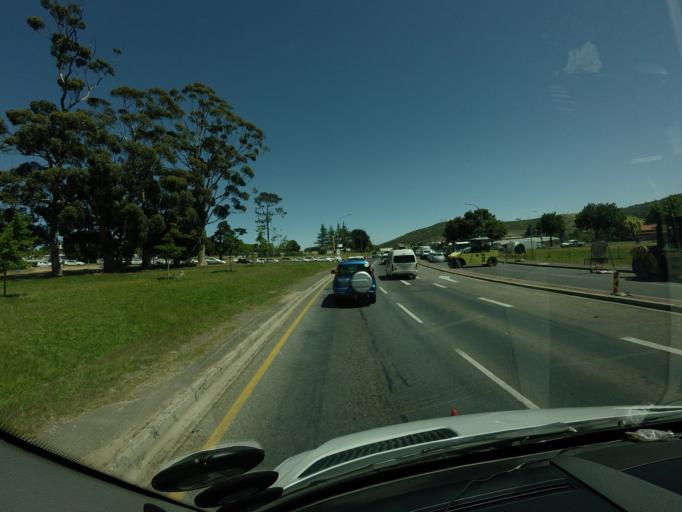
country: ZA
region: Western Cape
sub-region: Cape Winelands District Municipality
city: Stellenbosch
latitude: -33.9218
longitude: 18.8584
